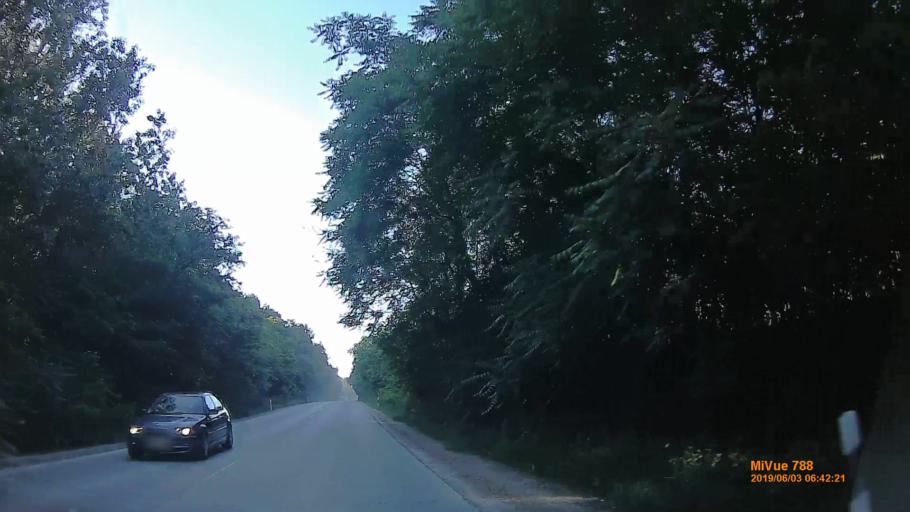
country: HU
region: Pest
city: Delegyhaza
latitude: 47.2672
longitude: 19.1141
